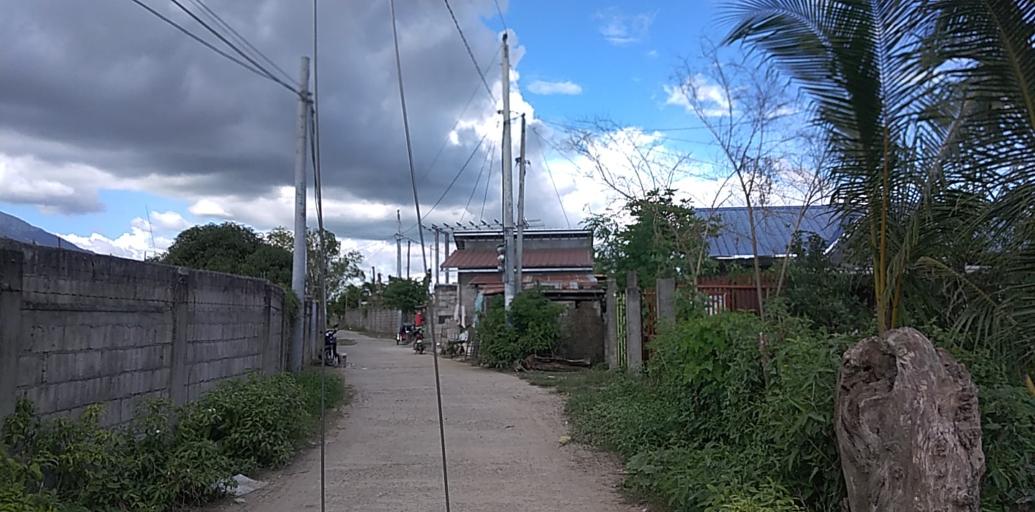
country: PH
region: Central Luzon
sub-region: Province of Pampanga
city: Arayat
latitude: 15.1352
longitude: 120.7824
